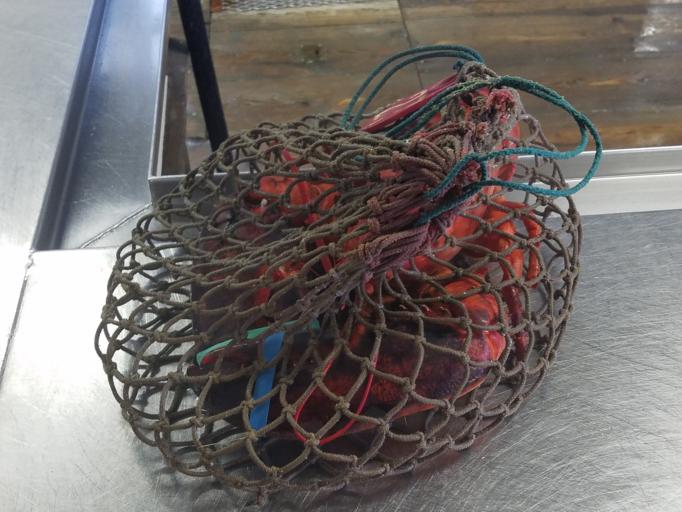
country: US
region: Maine
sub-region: Waldo County
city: Belfast
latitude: 44.4302
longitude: -68.9964
